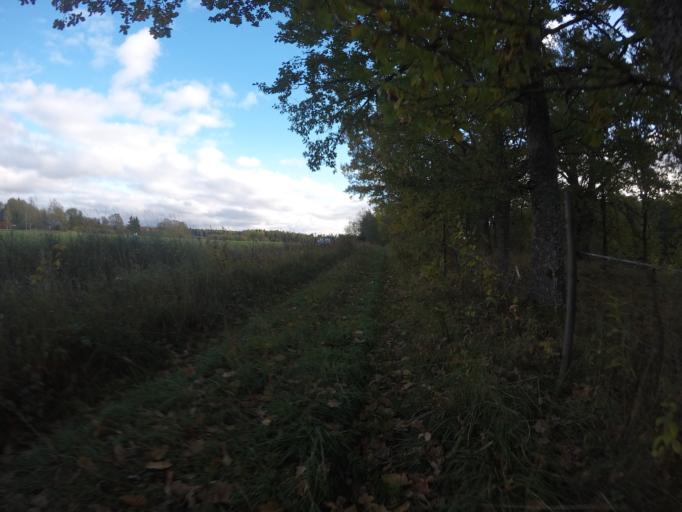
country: SE
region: Vaestmanland
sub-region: Arboga Kommun
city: Tyringe
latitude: 59.3274
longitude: 15.9716
